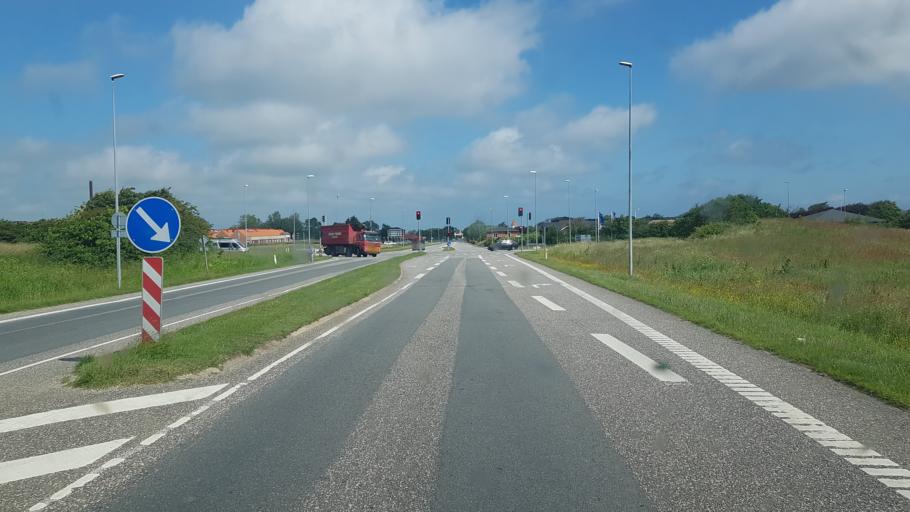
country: DK
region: Central Jutland
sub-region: Lemvig Kommune
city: Lemvig
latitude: 56.5388
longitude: 8.3061
